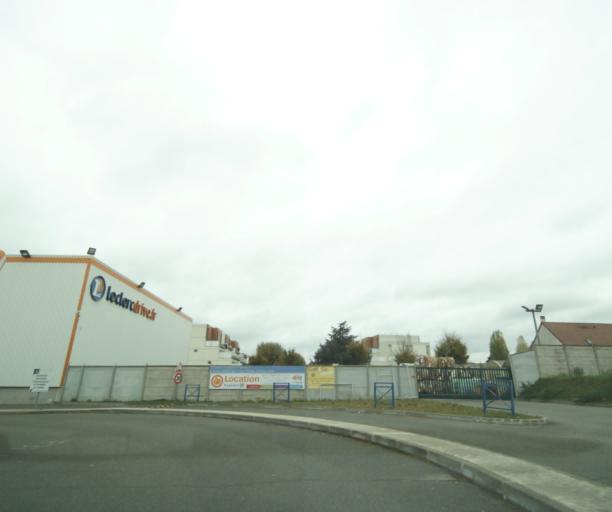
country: FR
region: Centre
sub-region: Departement d'Eure-et-Loir
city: Dreux
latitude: 48.7369
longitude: 1.3510
